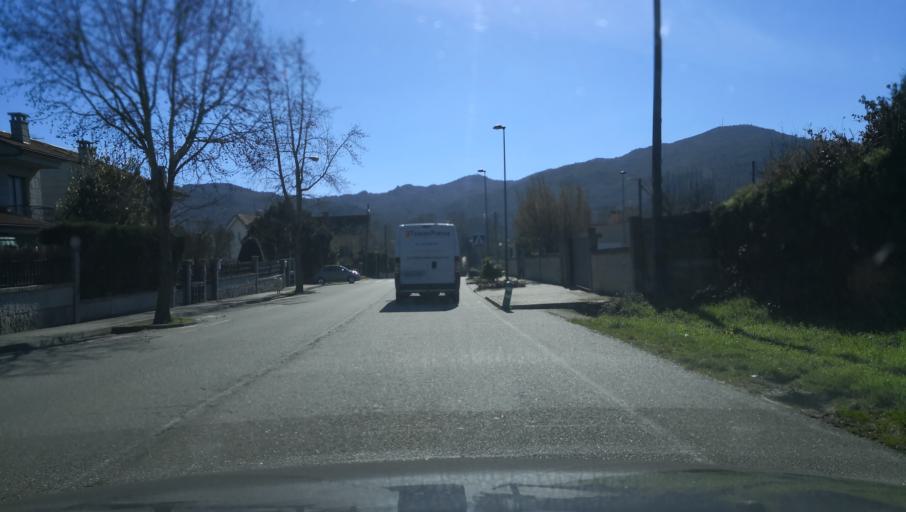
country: ES
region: Galicia
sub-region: Provincia de Ourense
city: Allariz
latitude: 42.1927
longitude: -7.8065
